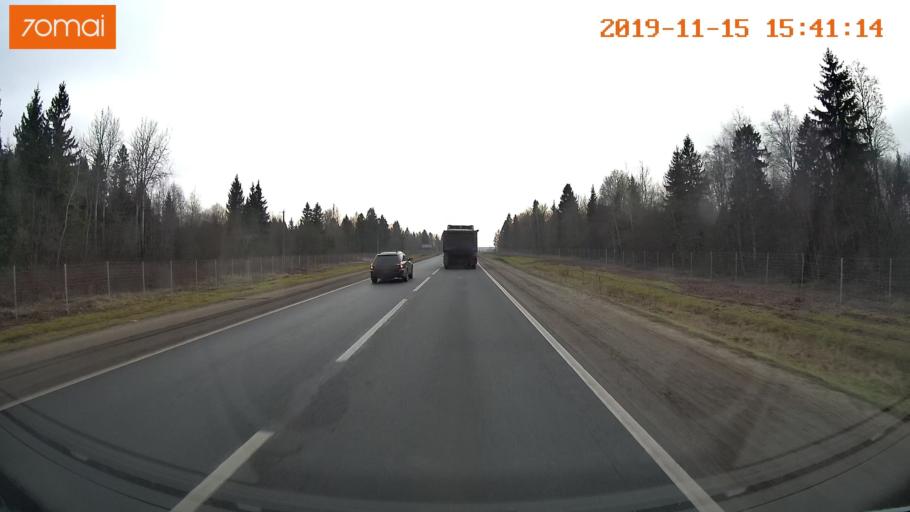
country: RU
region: Jaroslavl
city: Danilov
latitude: 58.0028
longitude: 40.0497
